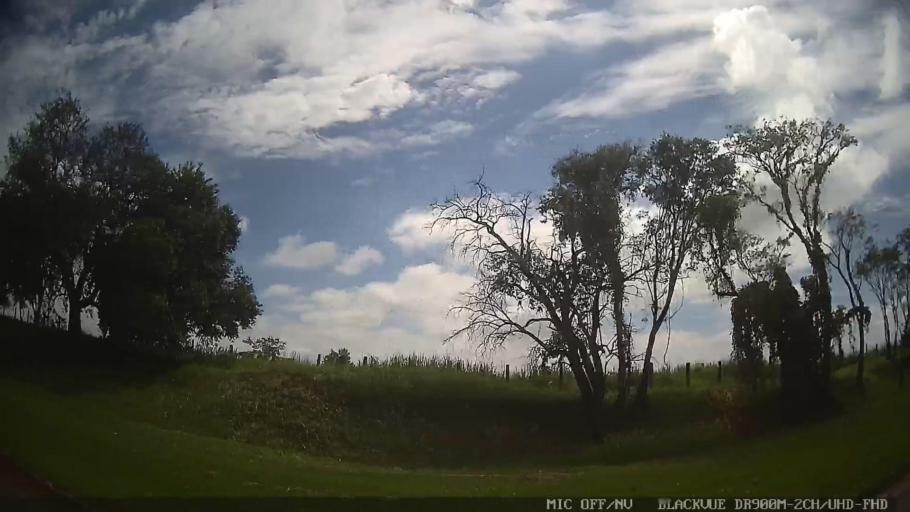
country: BR
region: Sao Paulo
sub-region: Tiete
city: Tiete
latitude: -23.0994
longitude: -47.7737
